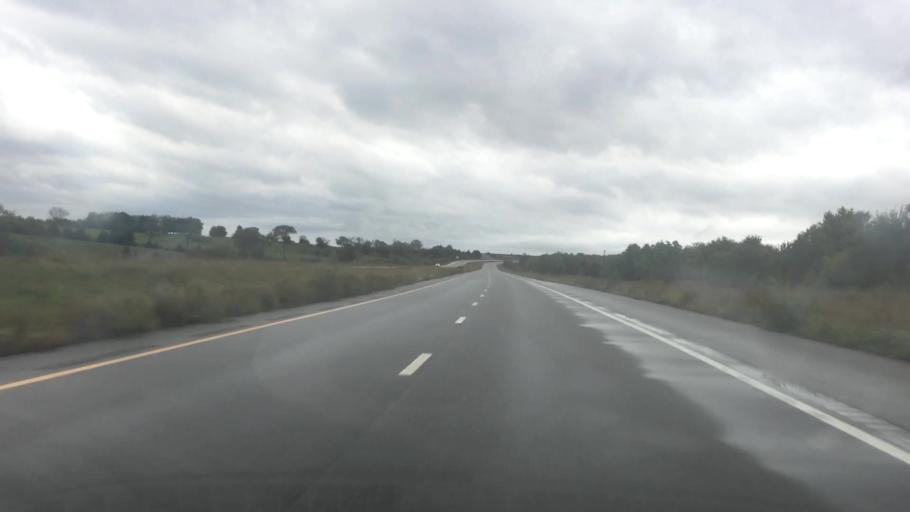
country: US
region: Kansas
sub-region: Miami County
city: Osawatomie
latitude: 38.4795
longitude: -94.9466
